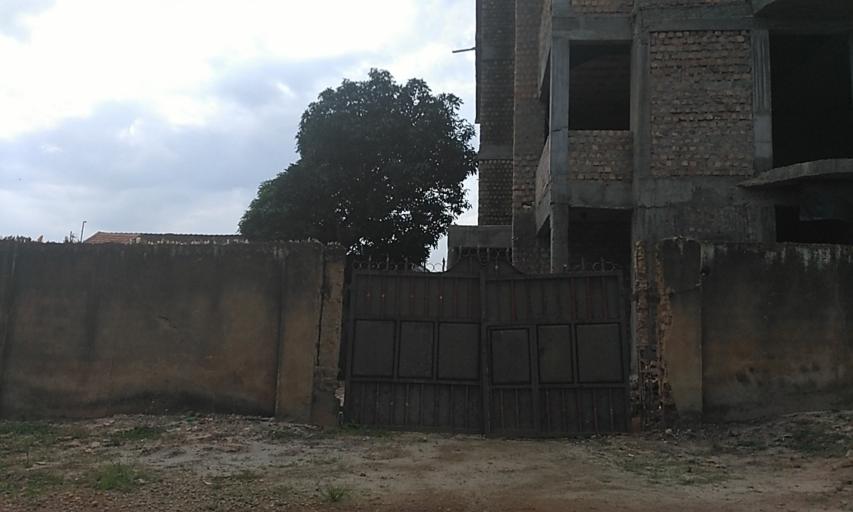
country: UG
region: Central Region
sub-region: Wakiso District
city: Kireka
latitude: 0.3433
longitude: 32.6202
